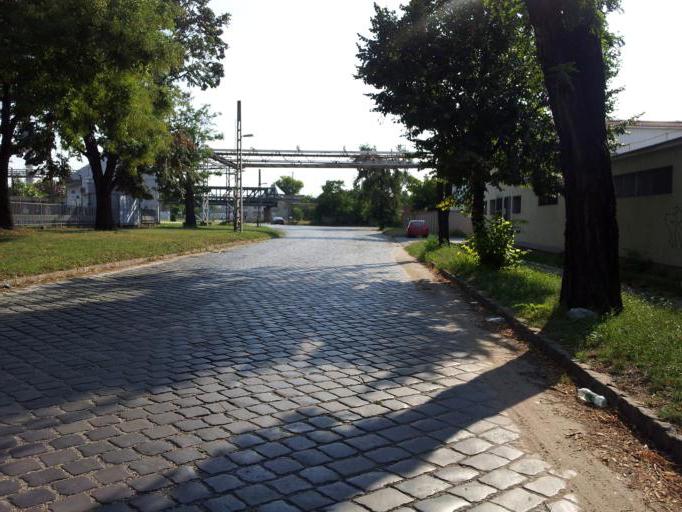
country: HU
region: Budapest
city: Budapest X. keruelet
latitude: 47.4753
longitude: 19.1302
